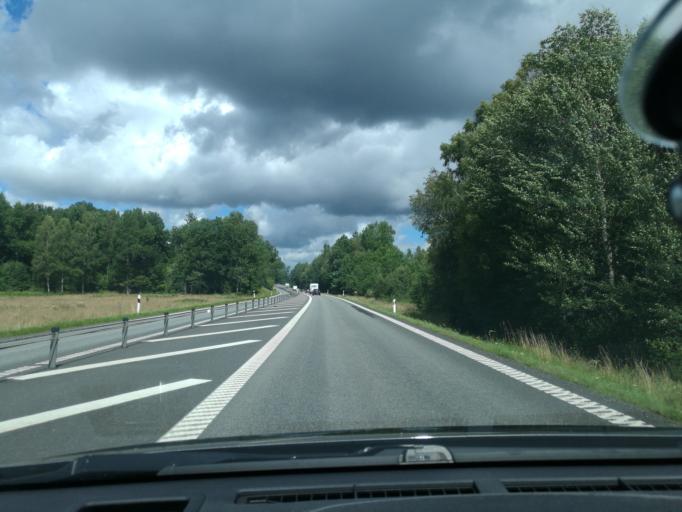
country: SE
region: Skane
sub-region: Osby Kommun
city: Osby
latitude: 56.3767
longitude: 14.0353
